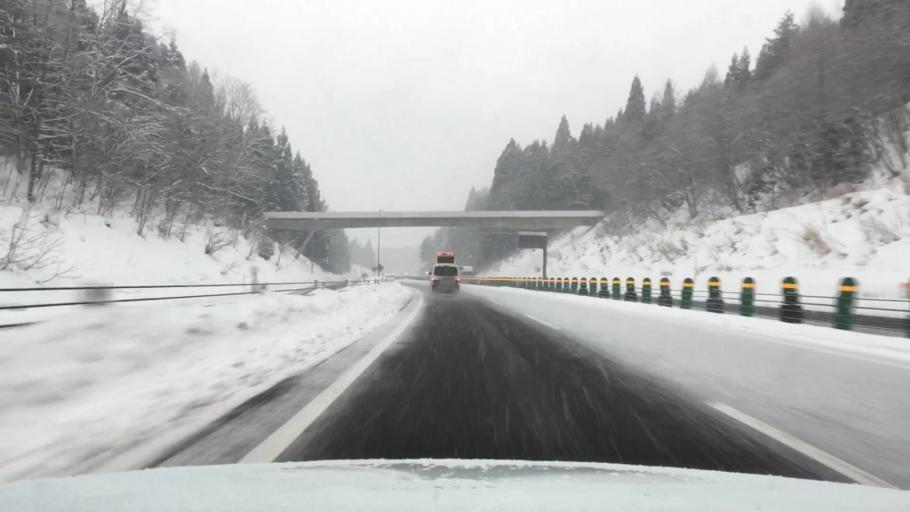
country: JP
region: Akita
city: Hanawa
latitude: 40.1636
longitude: 140.8034
